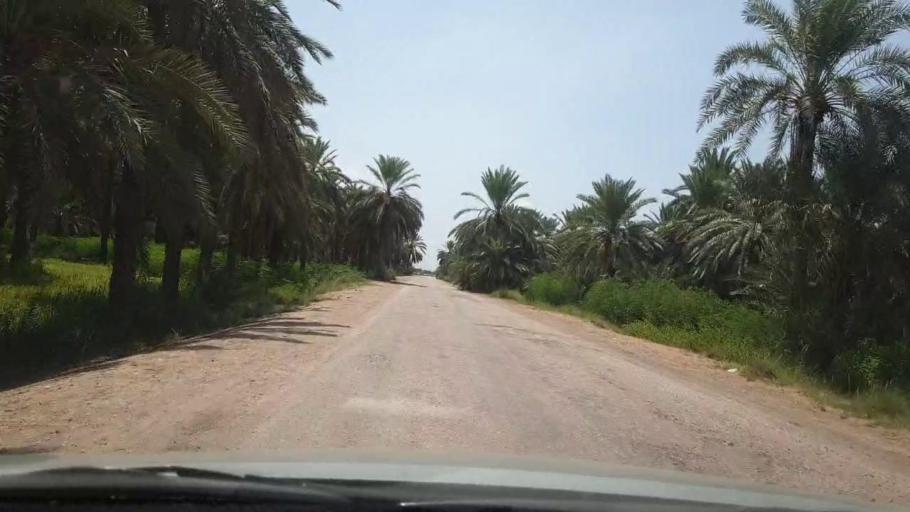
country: PK
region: Sindh
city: Pano Aqil
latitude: 27.6697
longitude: 69.0848
